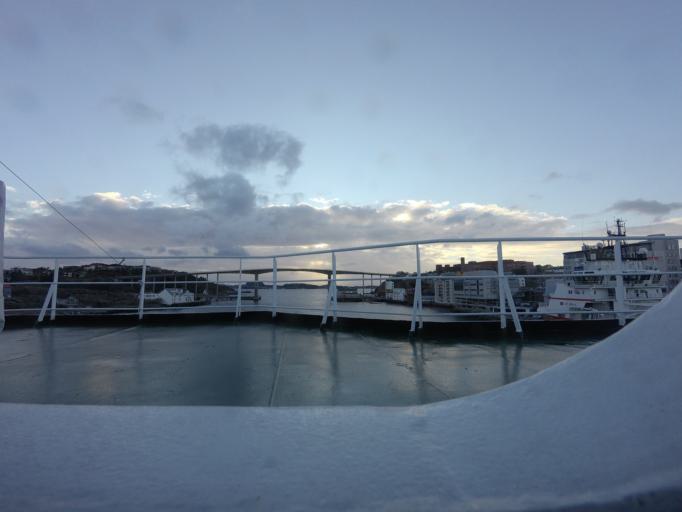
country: NO
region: More og Romsdal
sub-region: Kristiansund
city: Kristiansund
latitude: 63.1073
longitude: 7.7296
